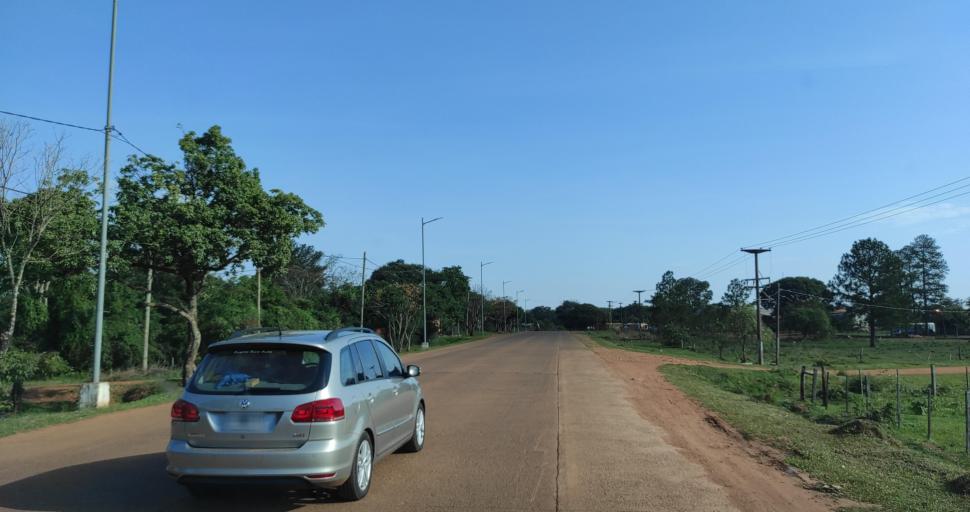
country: AR
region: Corrientes
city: Santo Tome
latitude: -28.5492
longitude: -56.0647
